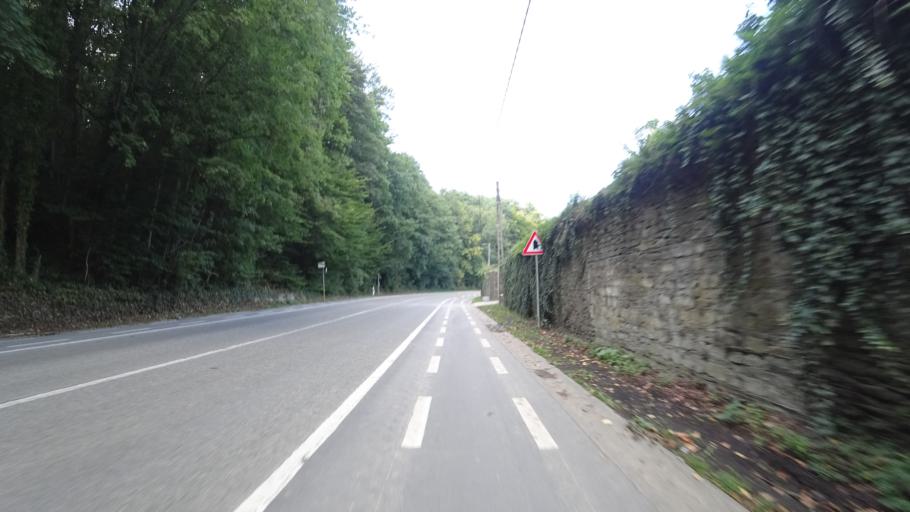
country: BE
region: Wallonia
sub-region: Province du Brabant Wallon
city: Villers-la-Ville
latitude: 50.5916
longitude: 4.5276
